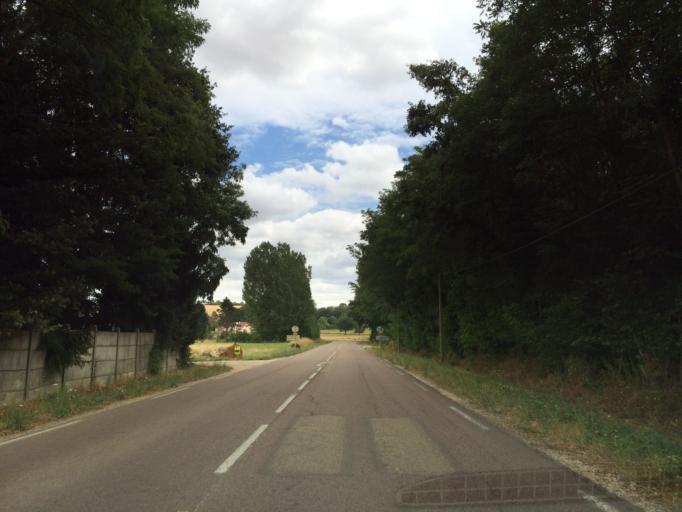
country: FR
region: Bourgogne
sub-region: Departement de l'Yonne
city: Fleury-la-Vallee
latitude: 47.8317
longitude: 3.4132
